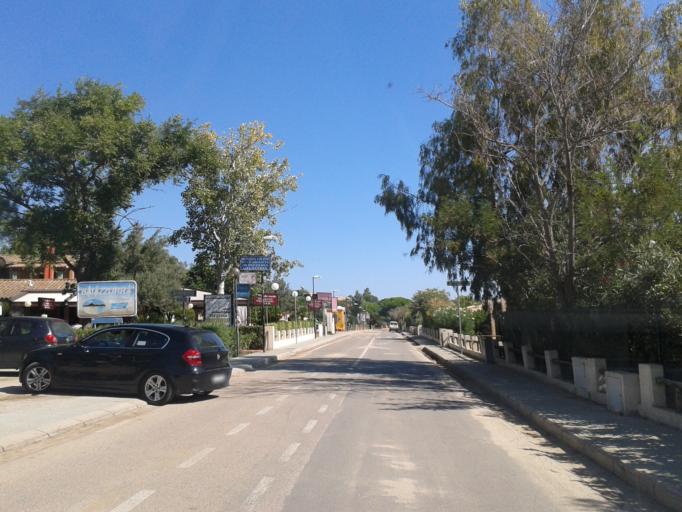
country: IT
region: Sardinia
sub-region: Provincia di Cagliari
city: Olia Speciosa
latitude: 39.2495
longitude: 9.5713
